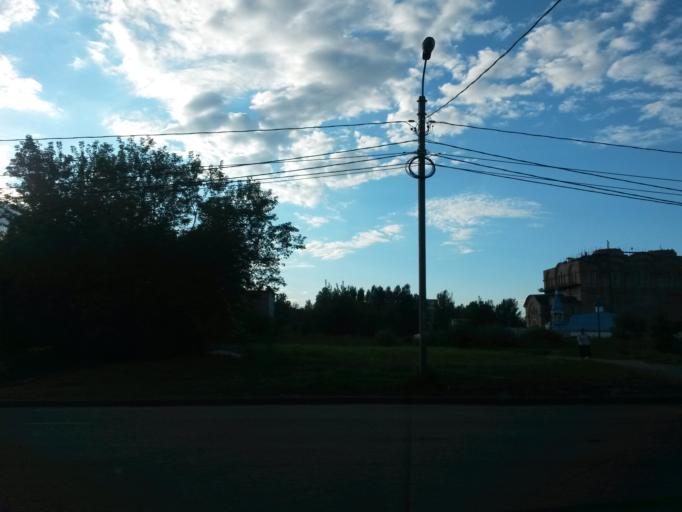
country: RU
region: Jaroslavl
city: Yaroslavl
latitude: 57.6883
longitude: 39.7769
